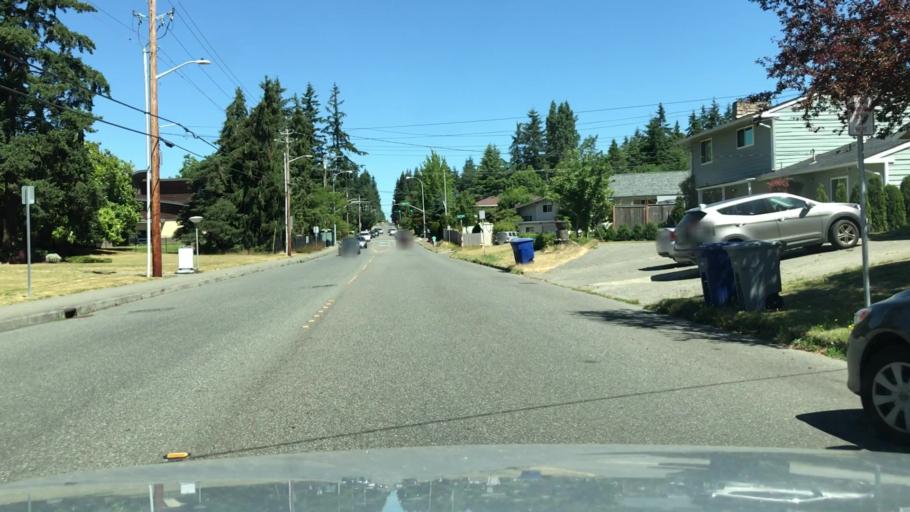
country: US
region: Washington
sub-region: King County
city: Eastgate
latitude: 47.6083
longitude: -122.1322
